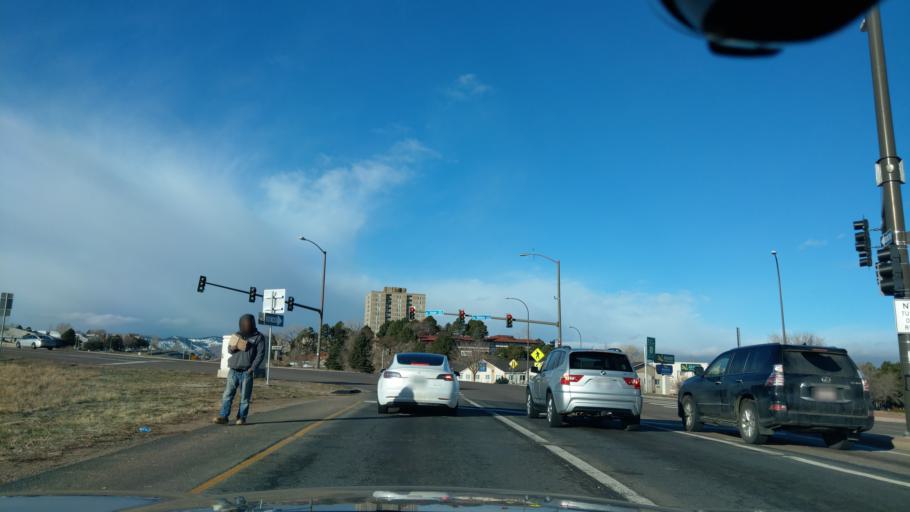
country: US
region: Colorado
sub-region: Jefferson County
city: Applewood
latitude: 39.7260
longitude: -105.1291
